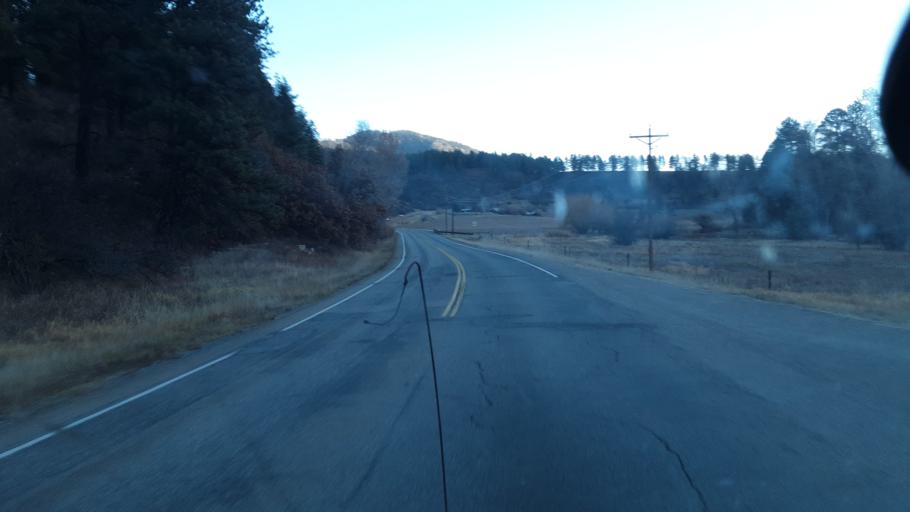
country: US
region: Colorado
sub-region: La Plata County
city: Durango
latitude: 37.3278
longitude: -107.7475
